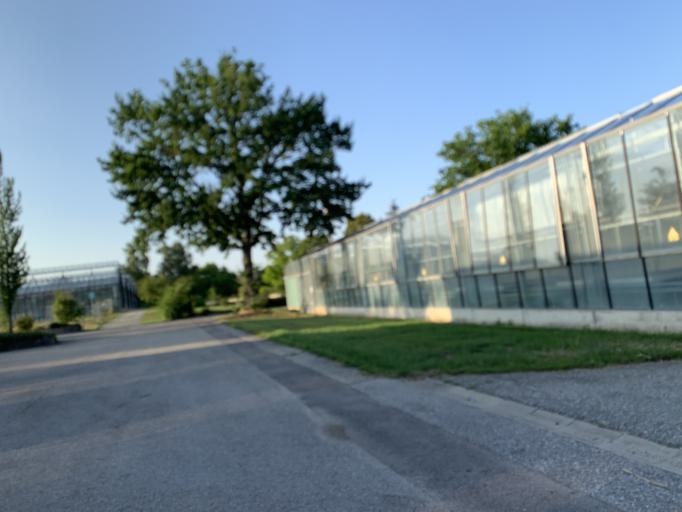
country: DE
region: Bavaria
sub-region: Upper Bavaria
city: Freising
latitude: 48.4025
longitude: 11.7310
